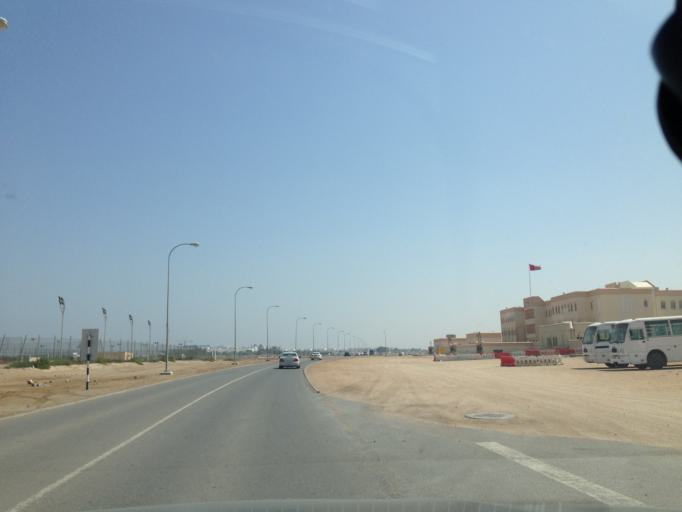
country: OM
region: Muhafazat Masqat
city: As Sib al Jadidah
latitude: 23.6306
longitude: 58.2503
